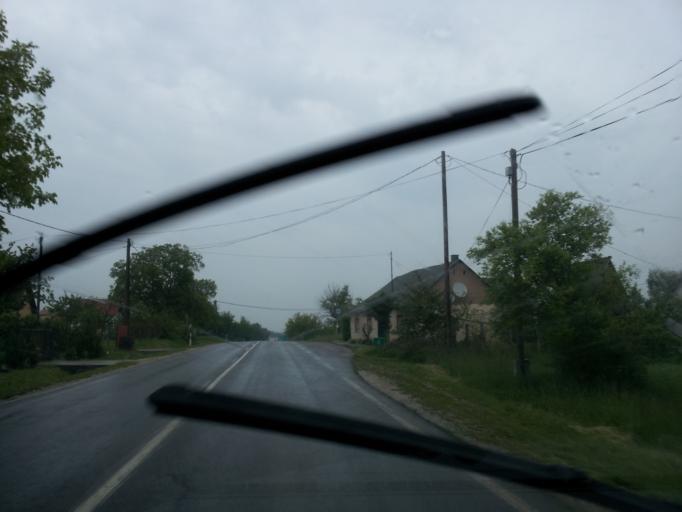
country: HU
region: Tolna
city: Szekszard
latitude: 46.3027
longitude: 18.6904
